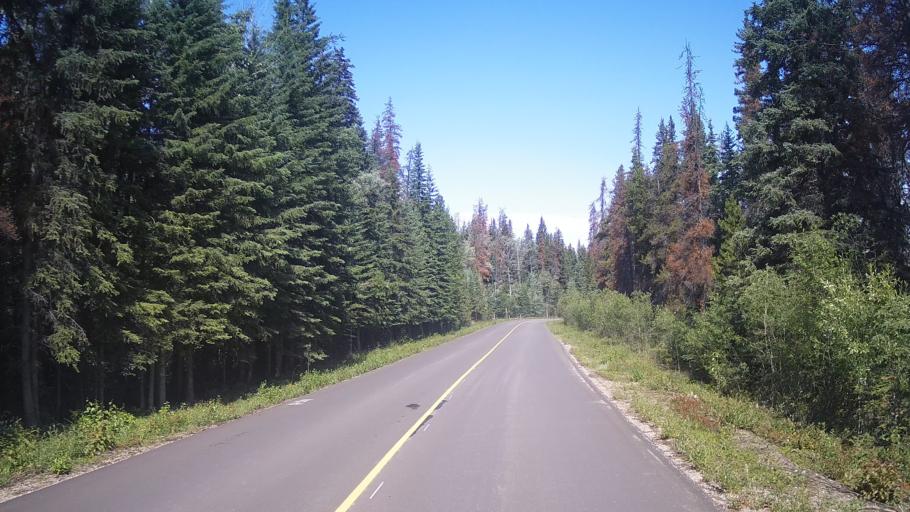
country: CA
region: Alberta
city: Jasper Park Lodge
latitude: 52.7439
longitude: -117.9694
